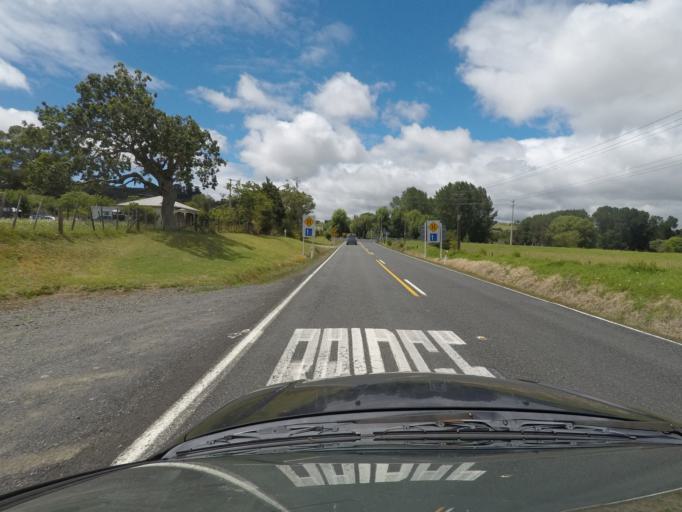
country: NZ
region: Northland
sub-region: Far North District
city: Kawakawa
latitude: -35.3643
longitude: 174.0895
